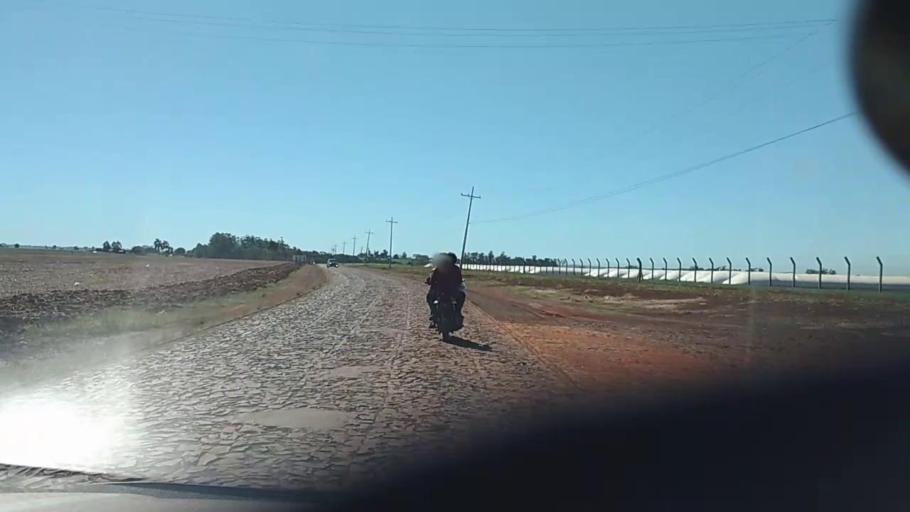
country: PY
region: Alto Parana
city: Naranjal
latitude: -25.9697
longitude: -55.1496
